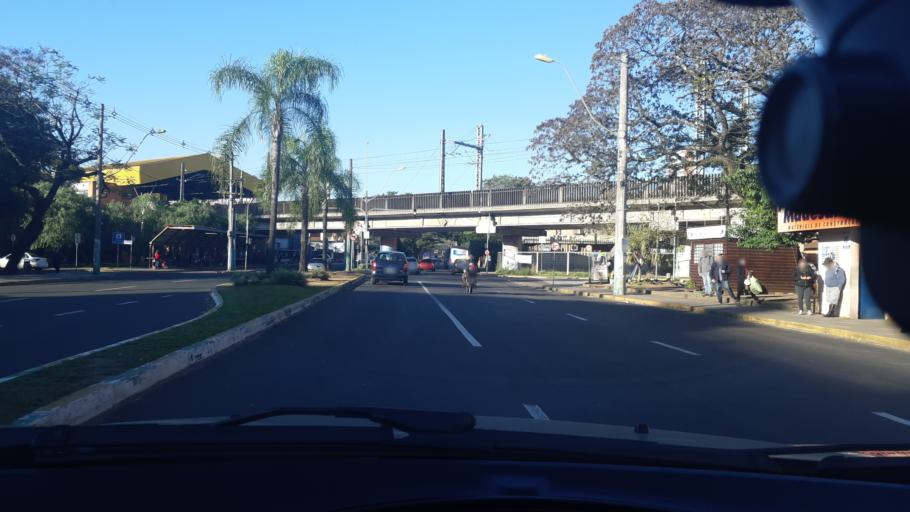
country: BR
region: Rio Grande do Sul
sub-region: Sao Leopoldo
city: Sao Leopoldo
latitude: -29.7705
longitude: -51.1428
